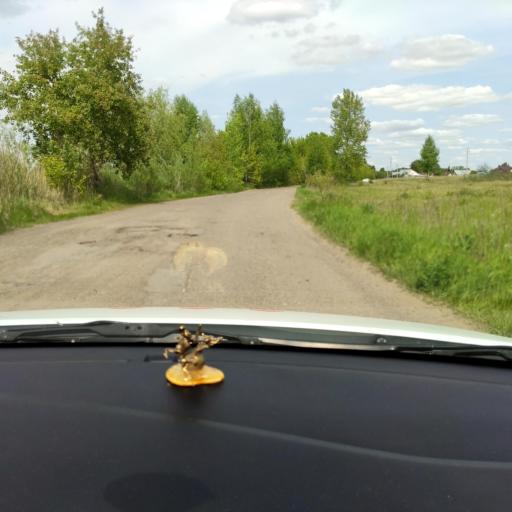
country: RU
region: Tatarstan
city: Verkhniy Uslon
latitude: 55.6975
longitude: 49.0589
